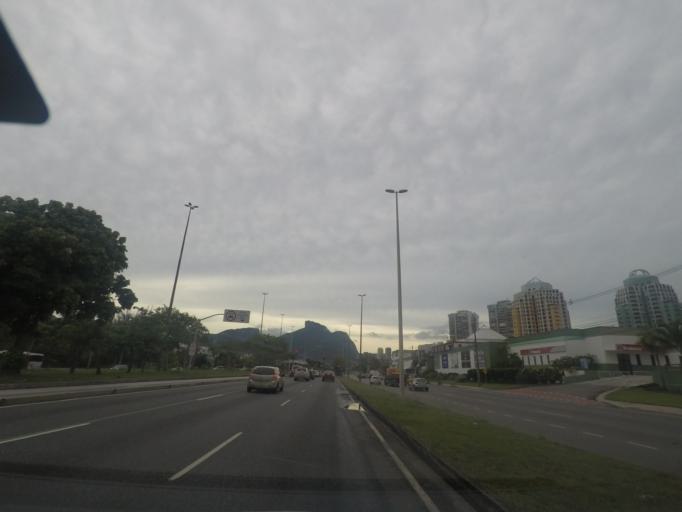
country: BR
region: Rio de Janeiro
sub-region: Rio De Janeiro
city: Rio de Janeiro
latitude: -23.0004
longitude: -43.3440
